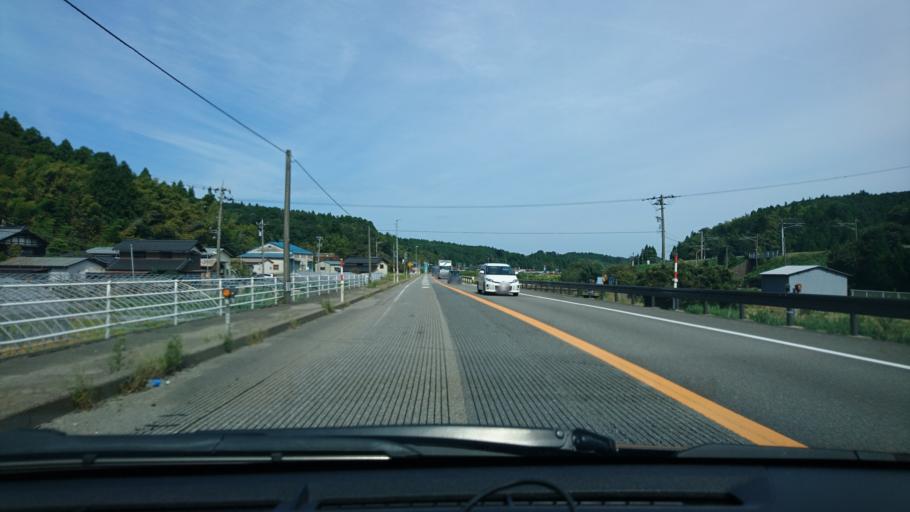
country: JP
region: Fukui
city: Maruoka
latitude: 36.2825
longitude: 136.2932
